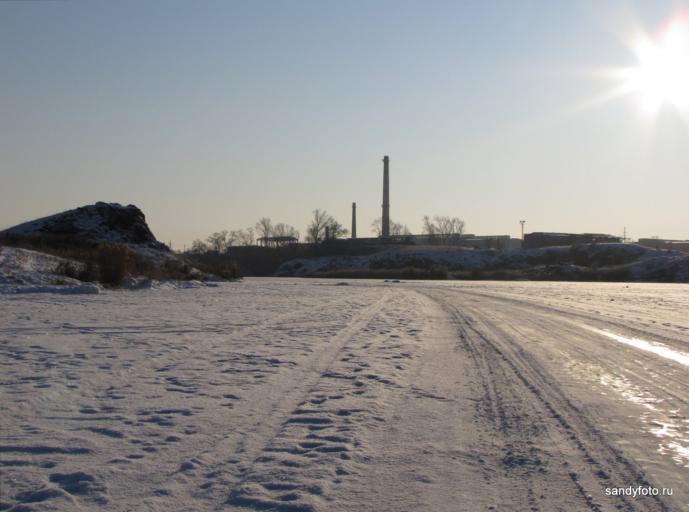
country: RU
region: Chelyabinsk
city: Troitsk
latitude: 54.0786
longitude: 61.5772
